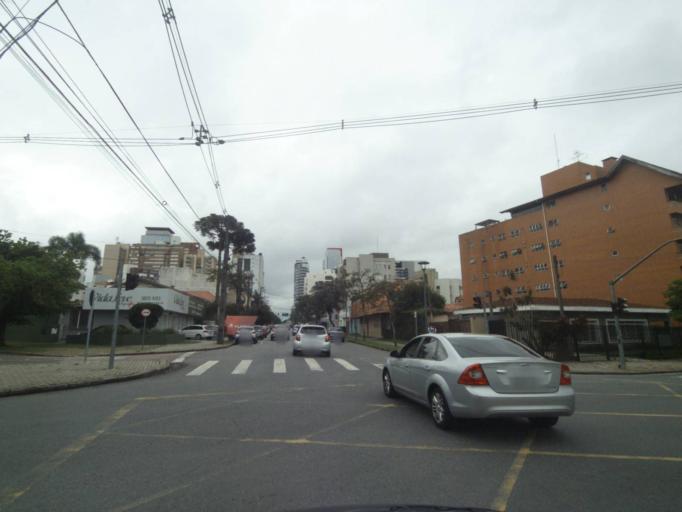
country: BR
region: Parana
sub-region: Curitiba
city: Curitiba
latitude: -25.4187
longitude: -49.2594
